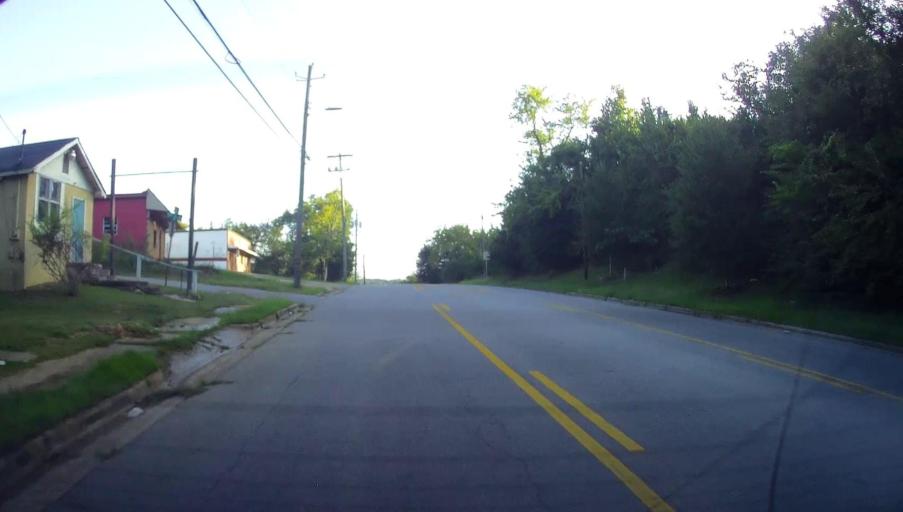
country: US
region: Alabama
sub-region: Russell County
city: Phenix City
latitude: 32.4466
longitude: -85.0092
